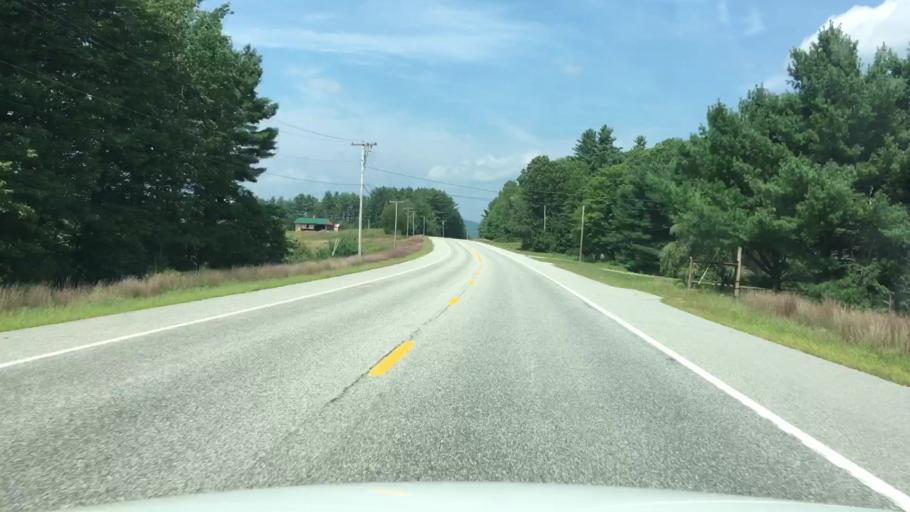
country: US
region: Maine
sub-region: Oxford County
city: Canton
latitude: 44.4555
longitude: -70.3184
